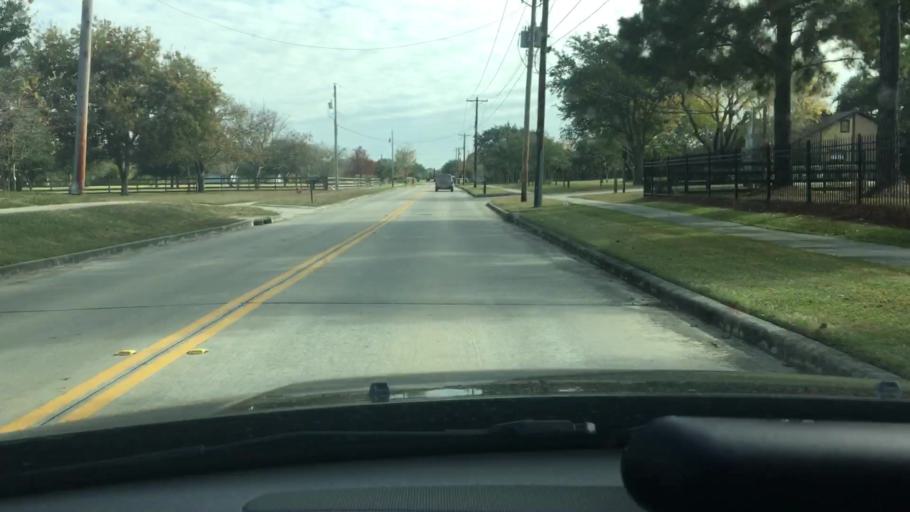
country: US
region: Texas
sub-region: Galveston County
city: League City
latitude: 29.5058
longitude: -95.0629
